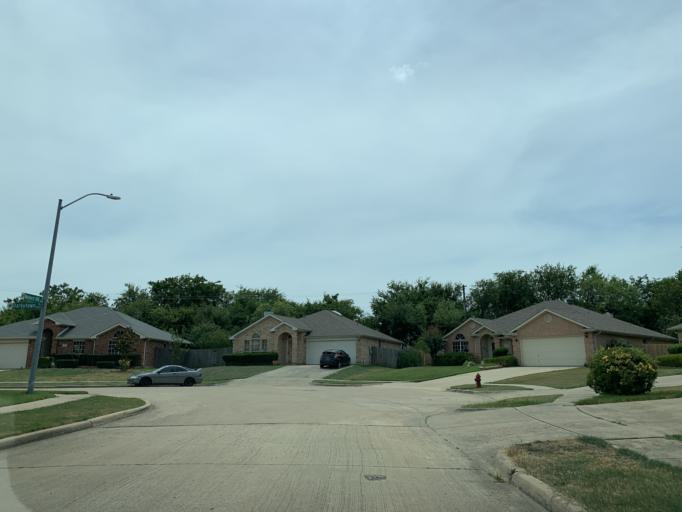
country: US
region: Texas
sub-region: Dallas County
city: Grand Prairie
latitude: 32.6615
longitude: -97.0236
